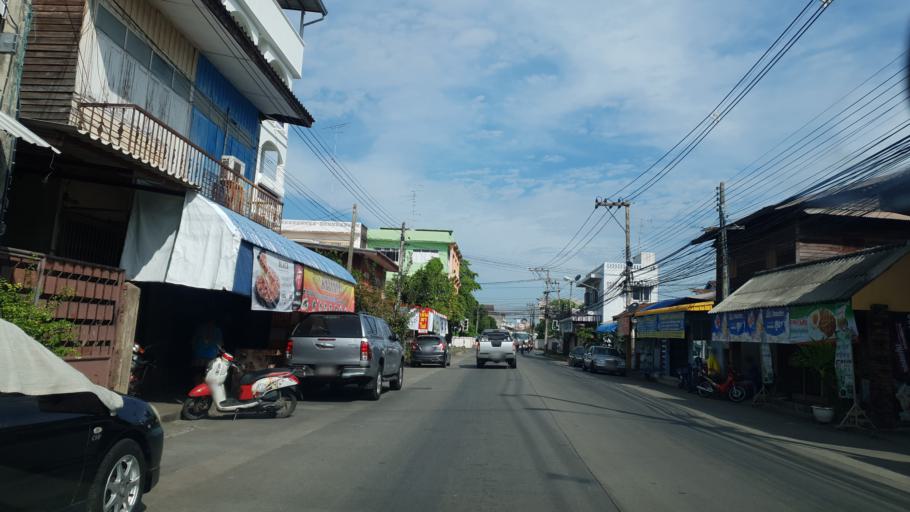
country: TH
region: Phitsanulok
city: Phitsanulok
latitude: 16.8099
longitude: 100.2676
